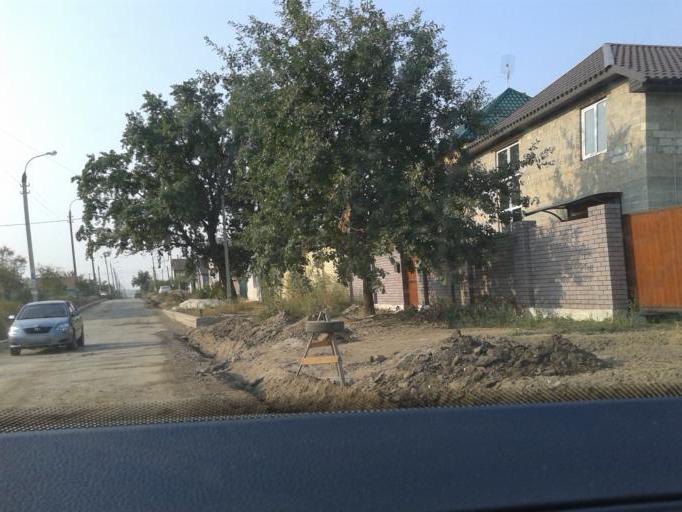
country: RU
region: Volgograd
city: Volgograd
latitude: 48.6143
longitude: 44.4139
